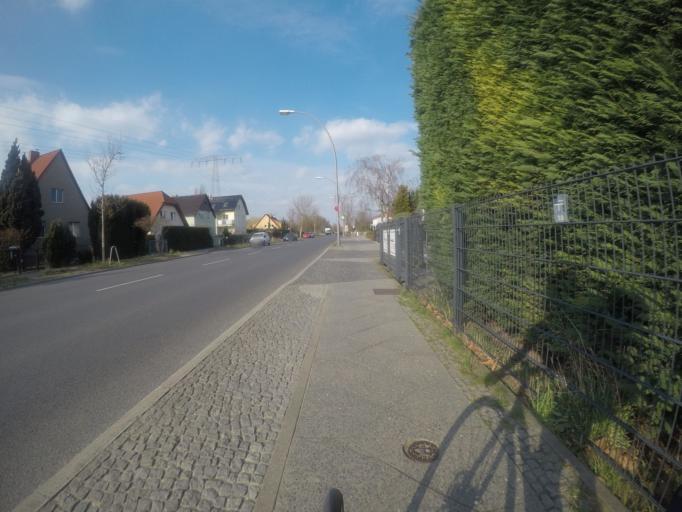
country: DE
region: Berlin
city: Altglienicke
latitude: 52.4080
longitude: 13.5259
